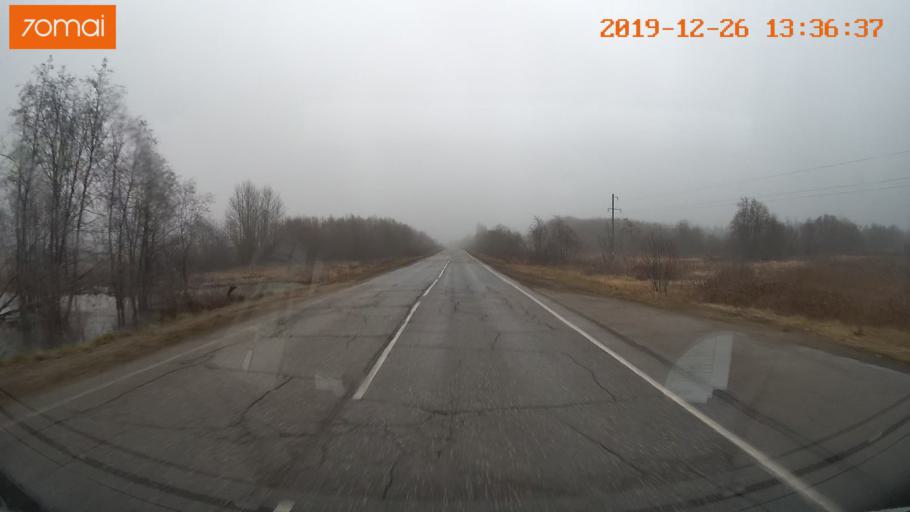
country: RU
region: Vologda
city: Sheksna
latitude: 58.7804
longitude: 38.3582
